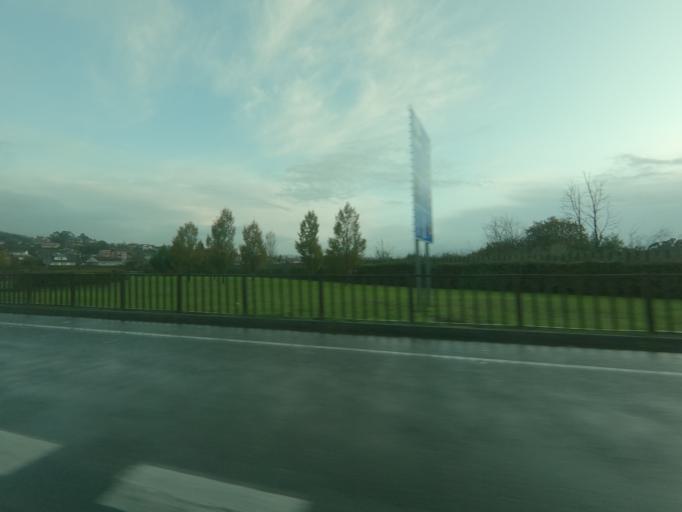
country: PT
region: Viana do Castelo
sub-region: Valenca
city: Valenca
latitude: 42.0356
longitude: -8.6556
